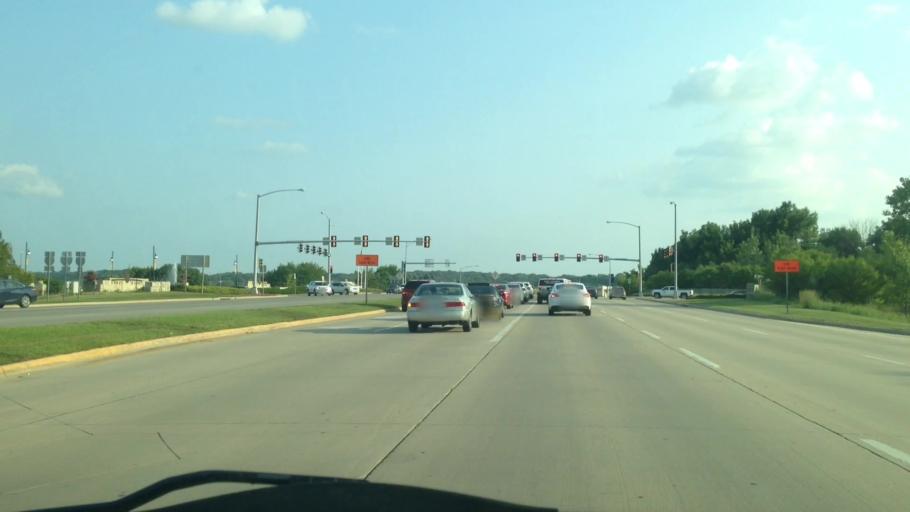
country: US
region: Iowa
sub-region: Johnson County
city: Coralville
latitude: 41.6933
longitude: -91.6086
